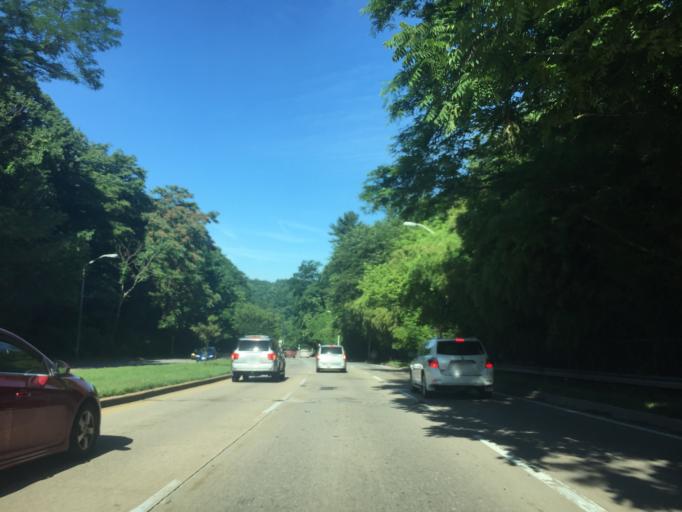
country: US
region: Maryland
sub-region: Baltimore County
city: Towson
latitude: 39.3624
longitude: -76.6408
